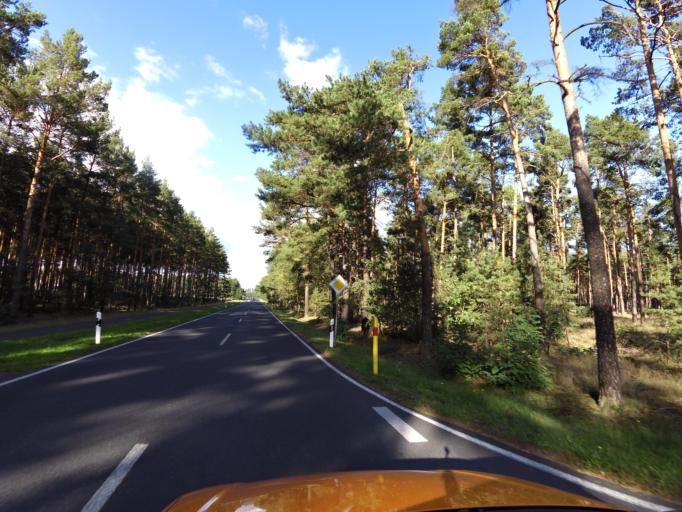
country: DE
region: Brandenburg
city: Luckenwalde
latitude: 52.1429
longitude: 13.1836
